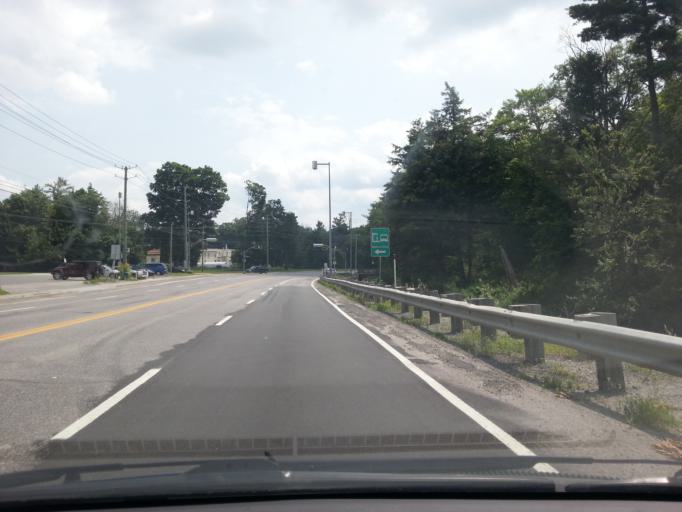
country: CA
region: Quebec
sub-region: Outaouais
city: Gatineau
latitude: 45.4927
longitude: -75.7542
